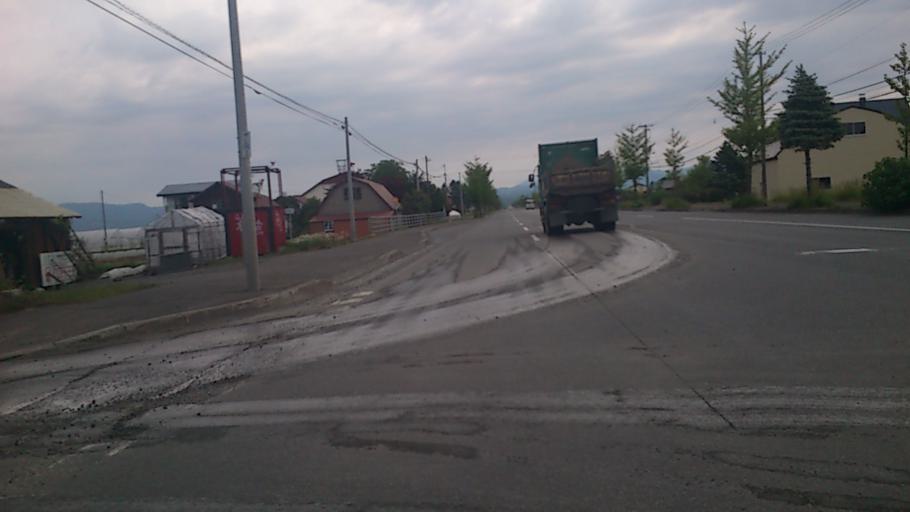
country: JP
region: Hokkaido
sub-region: Asahikawa-shi
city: Asahikawa
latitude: 43.8354
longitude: 142.4739
